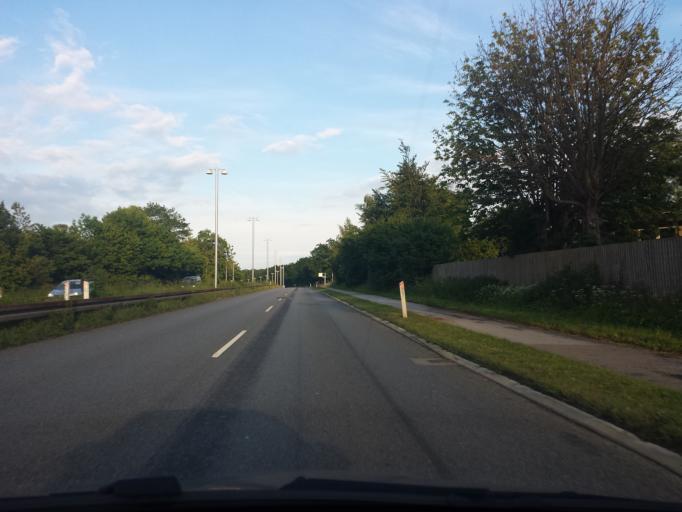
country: DK
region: Capital Region
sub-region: Ballerup Kommune
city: Ballerup
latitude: 55.7392
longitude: 12.3442
